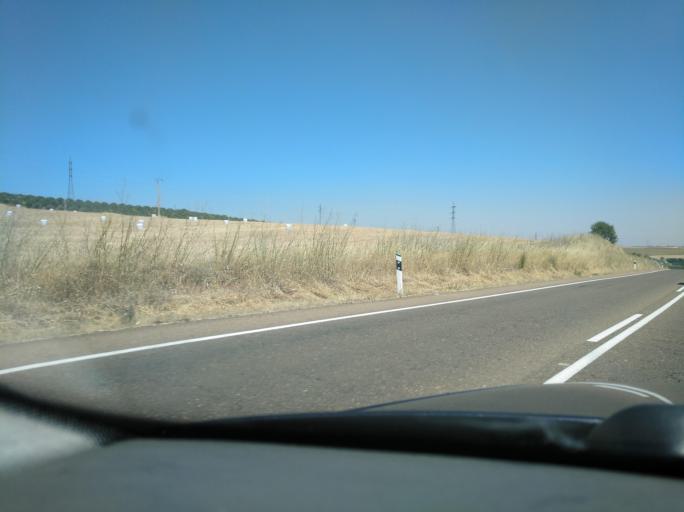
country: ES
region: Extremadura
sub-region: Provincia de Badajoz
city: Olivenza
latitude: 38.7312
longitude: -7.0714
